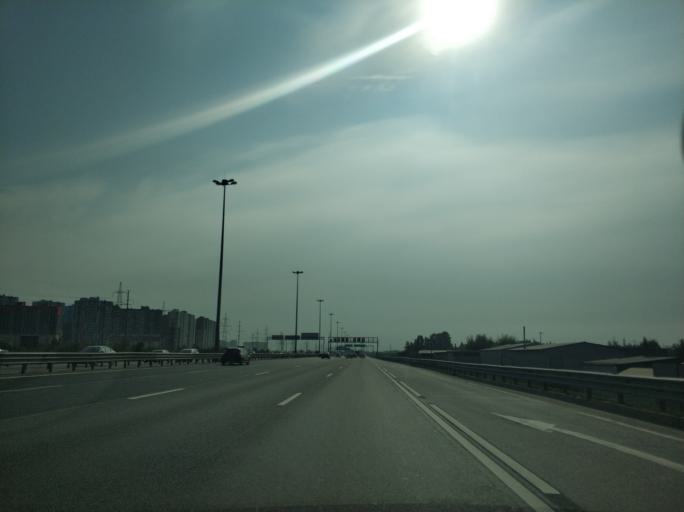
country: RU
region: Leningrad
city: Murino
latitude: 60.0316
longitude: 30.4436
